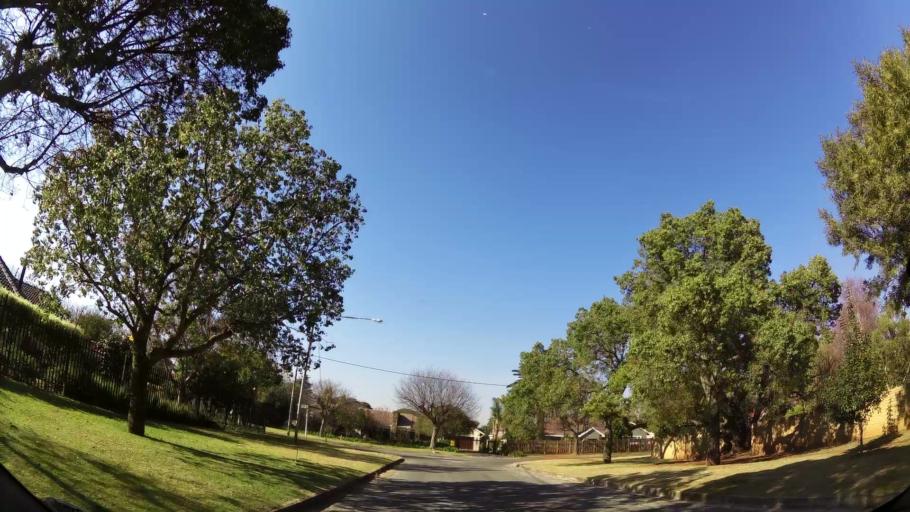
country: ZA
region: Gauteng
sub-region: Ekurhuleni Metropolitan Municipality
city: Benoni
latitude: -26.1511
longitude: 28.3212
